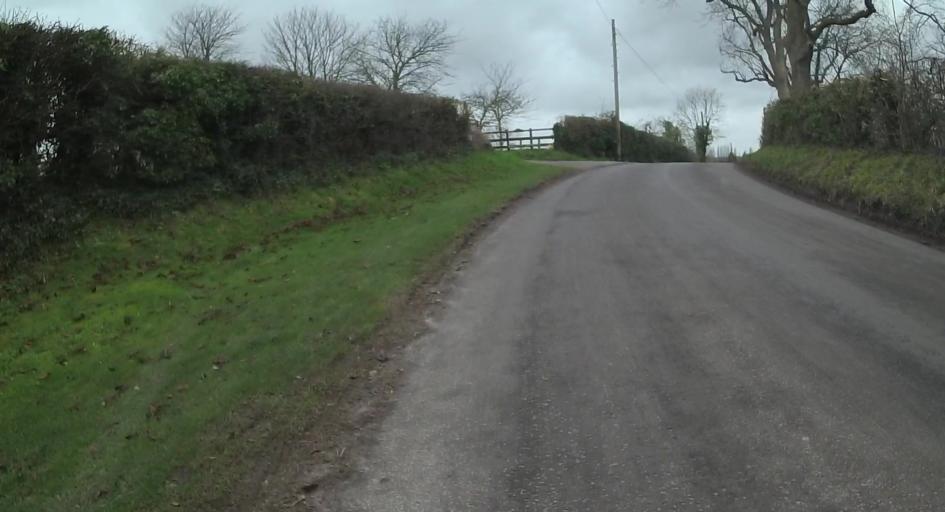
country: GB
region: England
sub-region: Hampshire
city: Kingsclere
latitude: 51.3296
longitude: -1.2798
